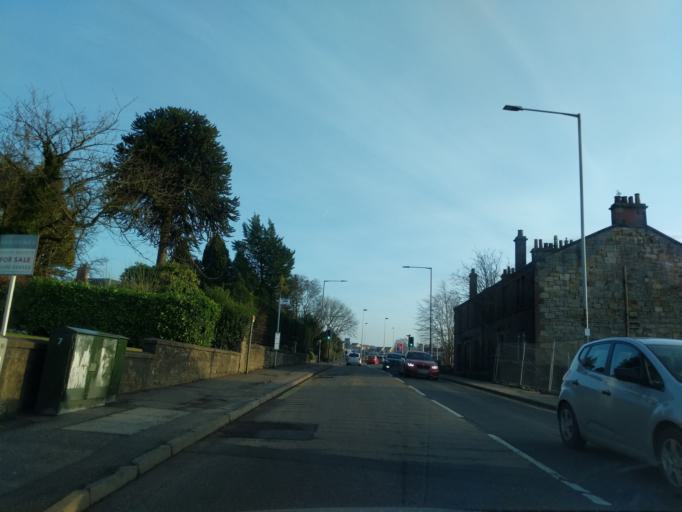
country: GB
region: Scotland
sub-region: South Lanarkshire
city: Carluke
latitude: 55.7300
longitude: -3.8367
